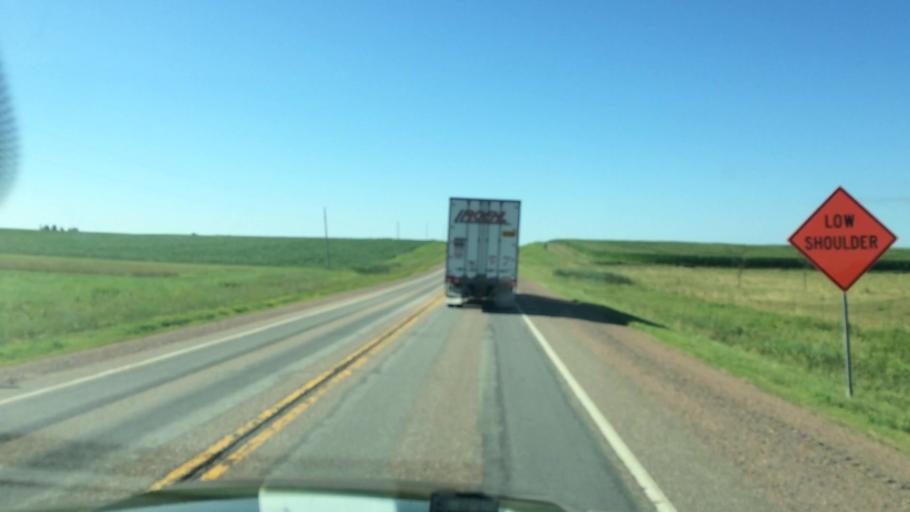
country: US
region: Wisconsin
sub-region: Marathon County
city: Athens
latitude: 44.9237
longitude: -90.0787
